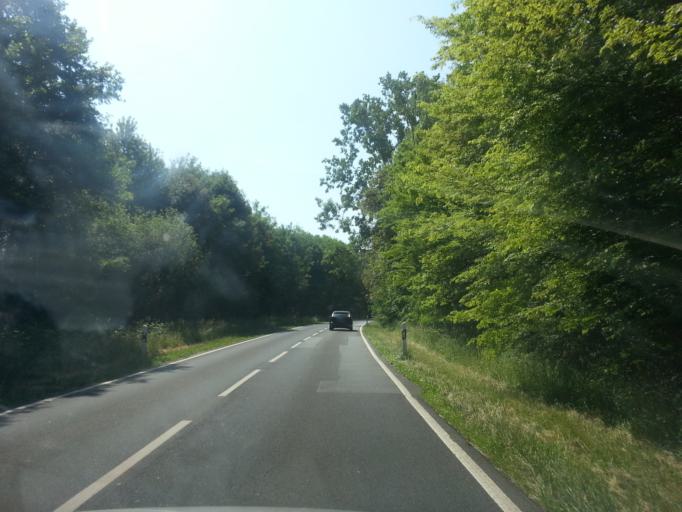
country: DE
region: Hesse
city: Dreieich
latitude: 50.0150
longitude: 8.7321
